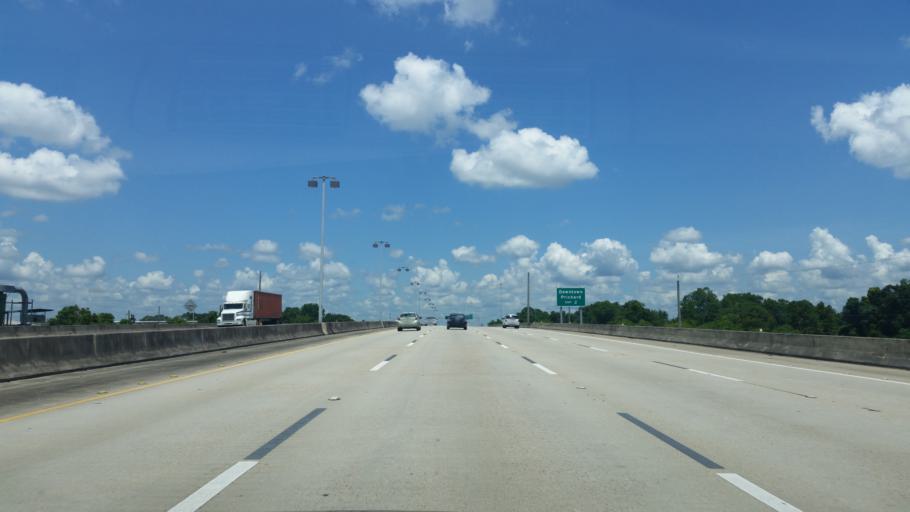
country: US
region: Alabama
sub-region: Mobile County
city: Prichard
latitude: 30.7224
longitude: -88.0662
